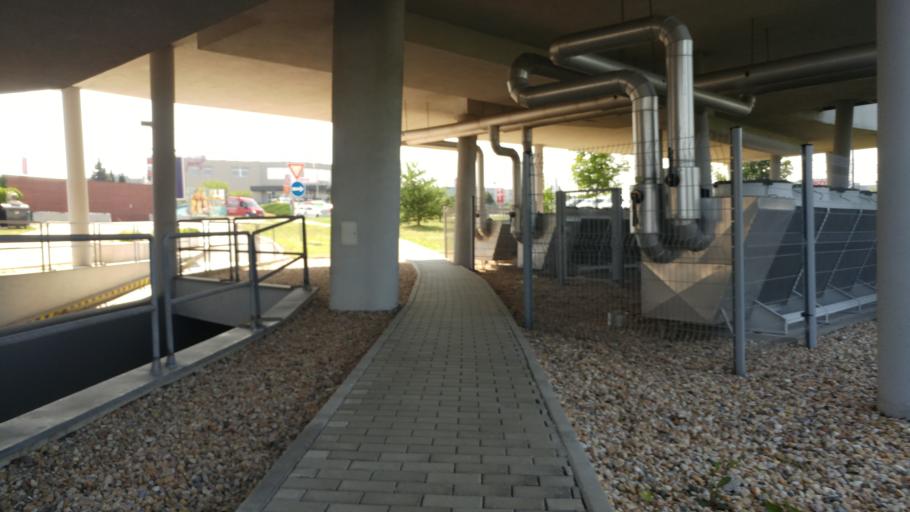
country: CZ
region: Central Bohemia
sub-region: Okres Praha-Zapad
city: Pruhonice
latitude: 50.0070
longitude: 14.5700
